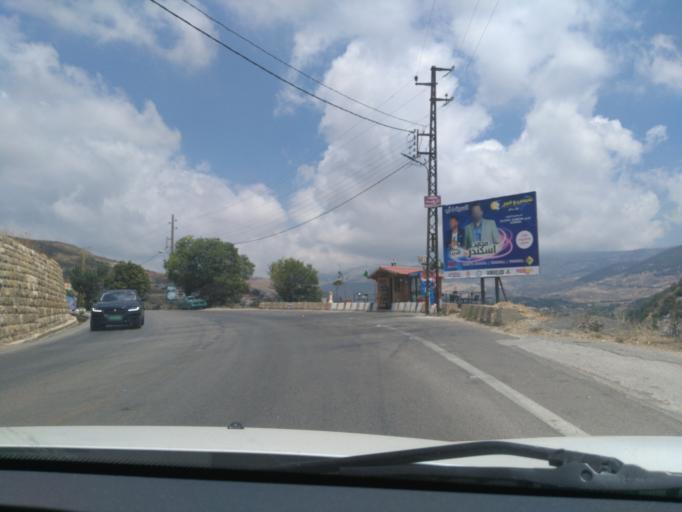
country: LB
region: Mont-Liban
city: Beit ed Dine
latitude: 33.7009
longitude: 35.6609
